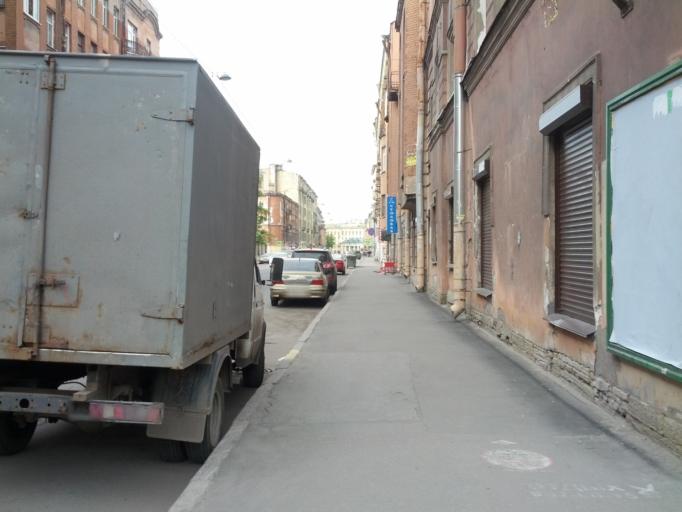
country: RU
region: St.-Petersburg
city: Centralniy
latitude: 59.9188
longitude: 30.3466
